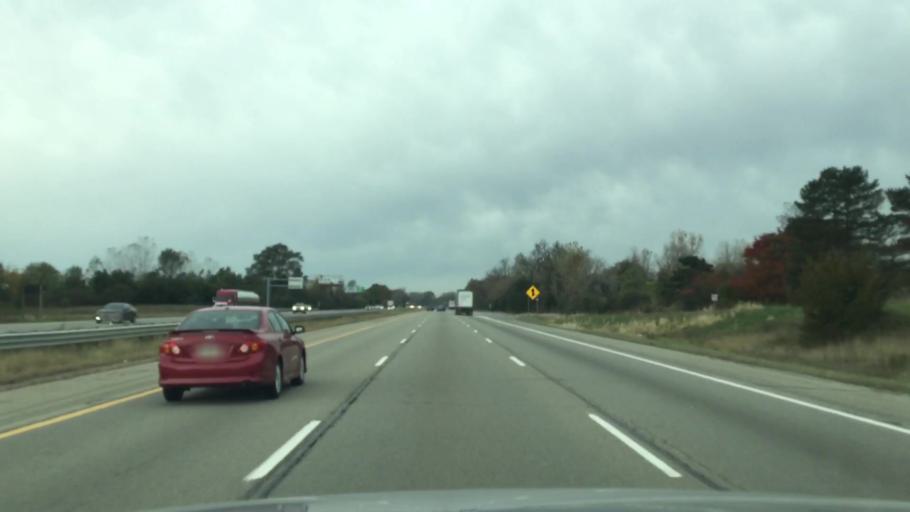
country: US
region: Michigan
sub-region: Washtenaw County
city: Dexter
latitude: 42.2919
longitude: -83.8399
